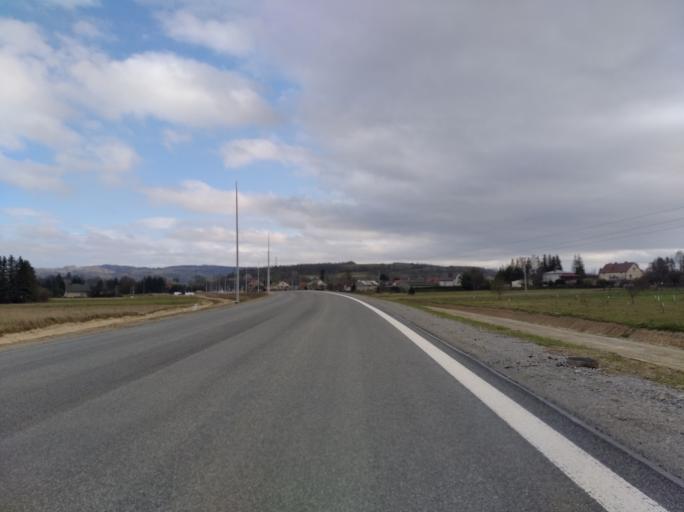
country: PL
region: Subcarpathian Voivodeship
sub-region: Powiat strzyzowski
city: Strzyzow
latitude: 49.8618
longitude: 21.7867
